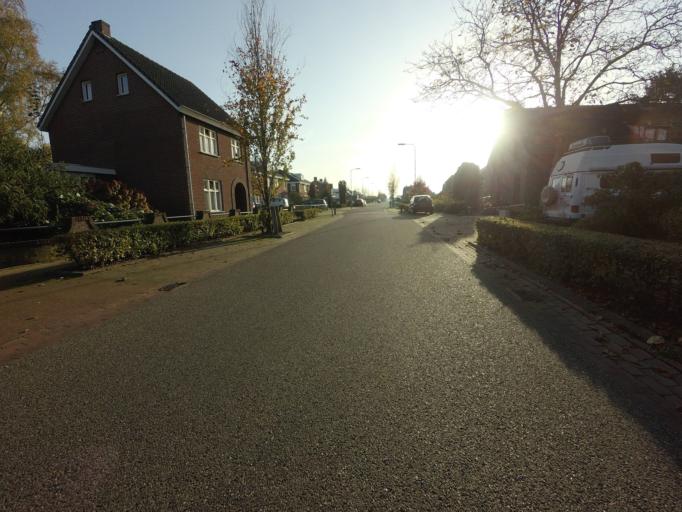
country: DE
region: North Rhine-Westphalia
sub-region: Regierungsbezirk Koln
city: Waldfeucht
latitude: 51.0816
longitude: 5.9650
